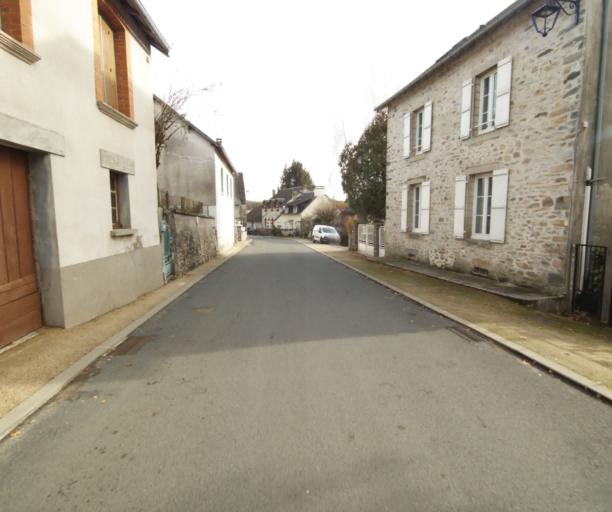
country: FR
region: Limousin
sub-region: Departement de la Correze
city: Beynat
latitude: 45.1708
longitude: 1.7348
